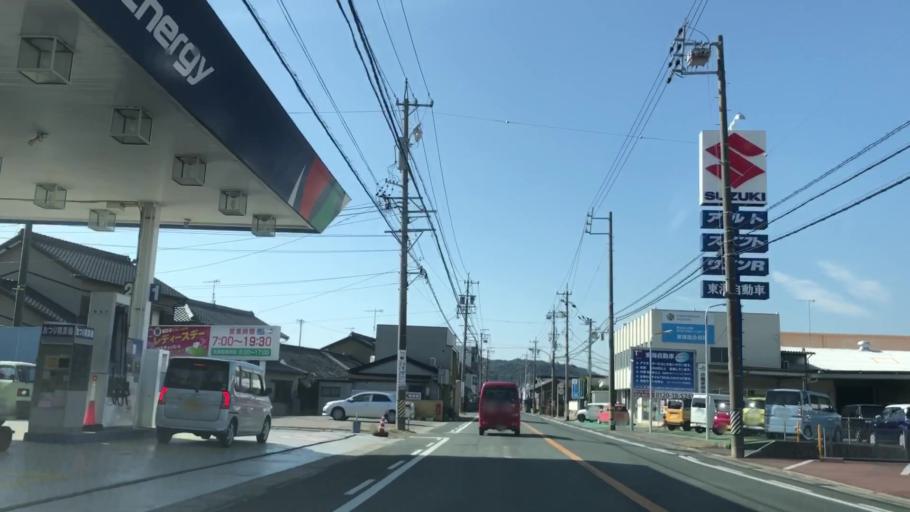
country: JP
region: Aichi
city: Gamagori
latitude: 34.8148
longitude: 137.1920
